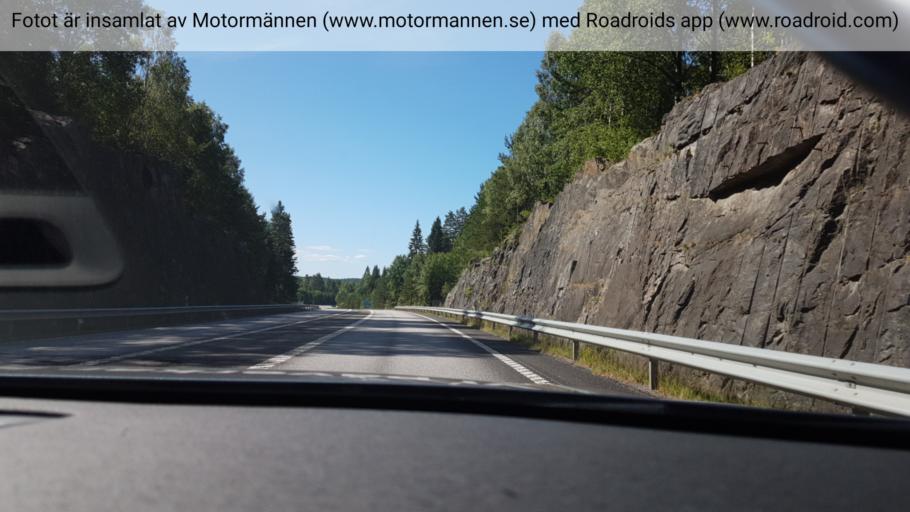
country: SE
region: Vaestra Goetaland
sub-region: Boras Kommun
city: Viskafors
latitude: 57.5936
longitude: 12.8665
